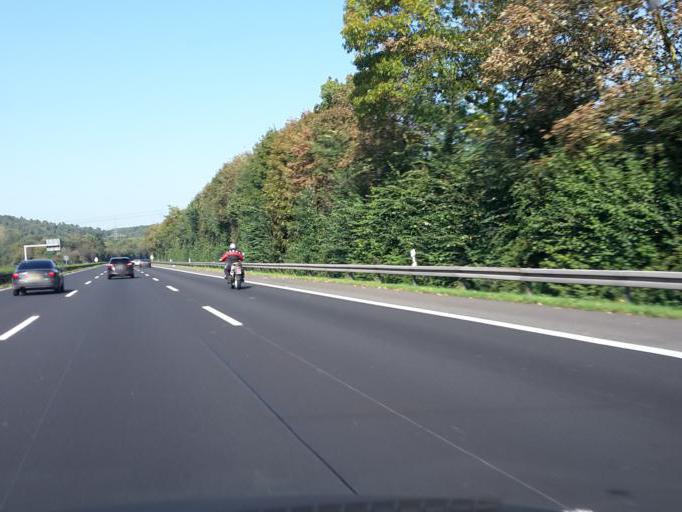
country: DE
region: North Rhine-Westphalia
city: Lohmar
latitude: 50.8330
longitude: 7.2024
